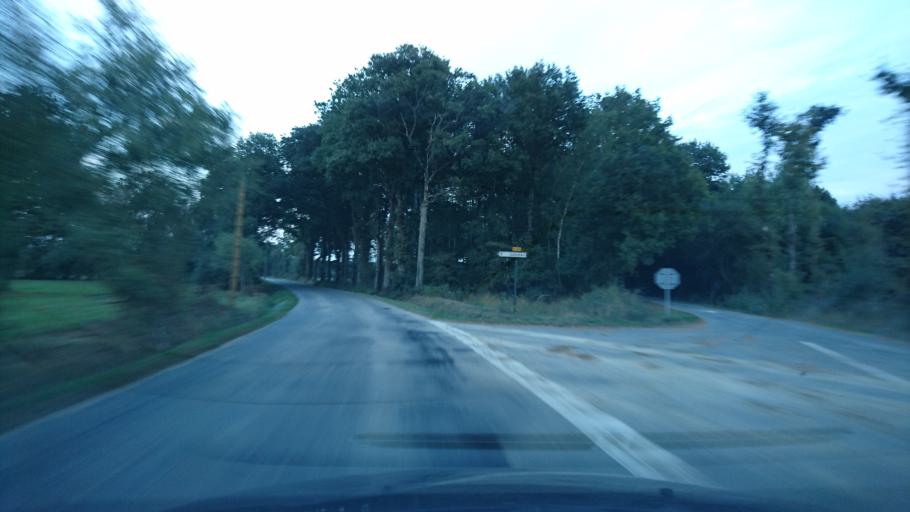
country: FR
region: Brittany
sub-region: Departement d'Ille-et-Vilaine
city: Pipriac
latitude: 47.8568
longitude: -1.9066
